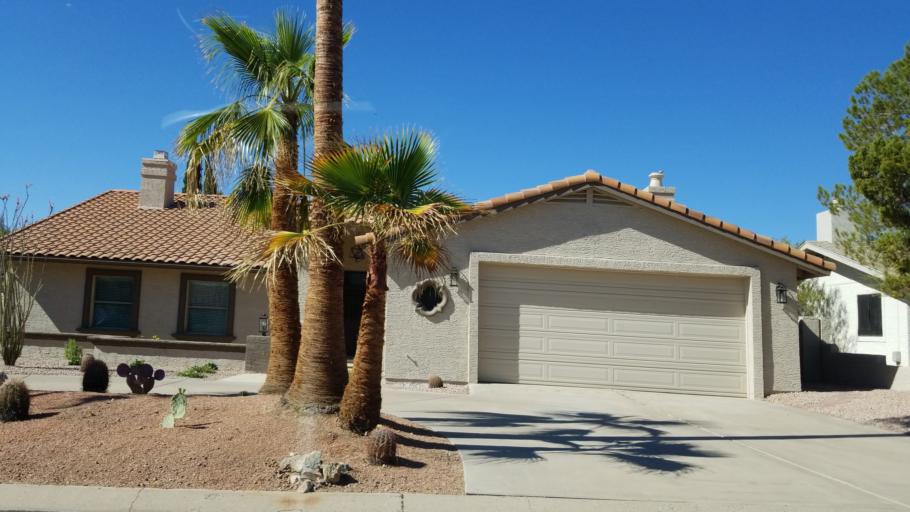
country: US
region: Arizona
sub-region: Maricopa County
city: Fountain Hills
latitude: 33.5952
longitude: -111.7553
